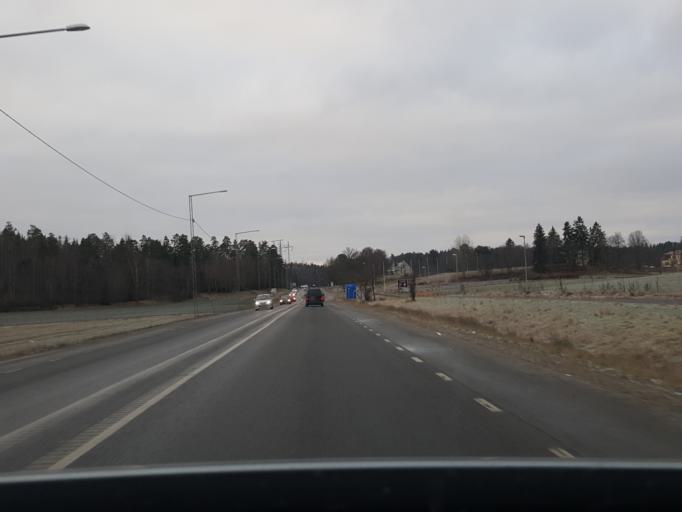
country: SE
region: Stockholm
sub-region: Botkyrka Kommun
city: Alby
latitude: 59.2243
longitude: 17.8374
